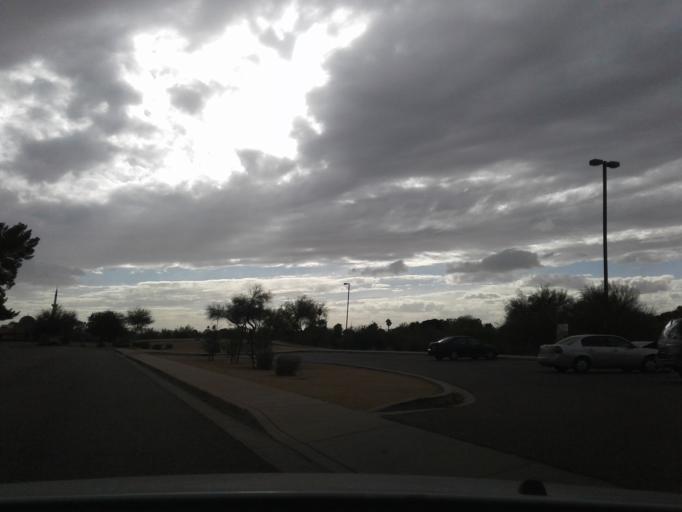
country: US
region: Arizona
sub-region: Maricopa County
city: Glendale
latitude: 33.6104
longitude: -112.1075
